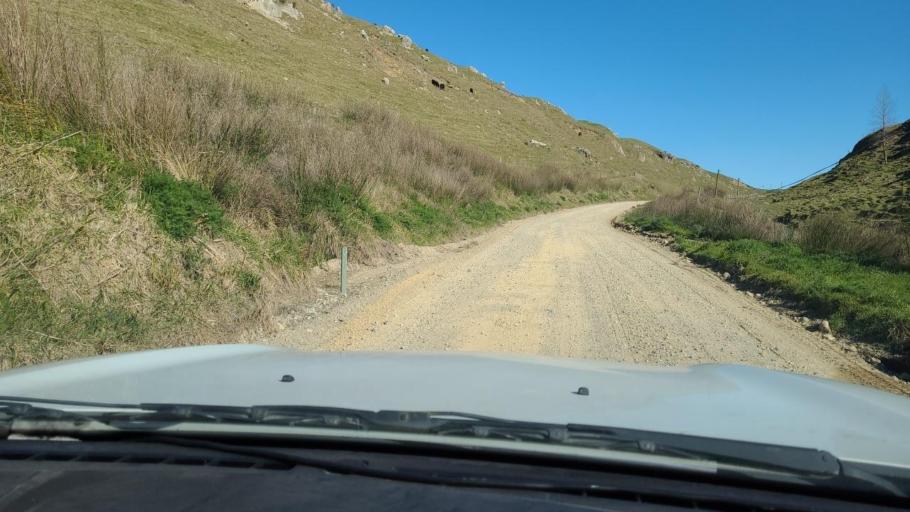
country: NZ
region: Hawke's Bay
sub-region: Hastings District
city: Hastings
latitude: -39.8118
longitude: 176.9689
